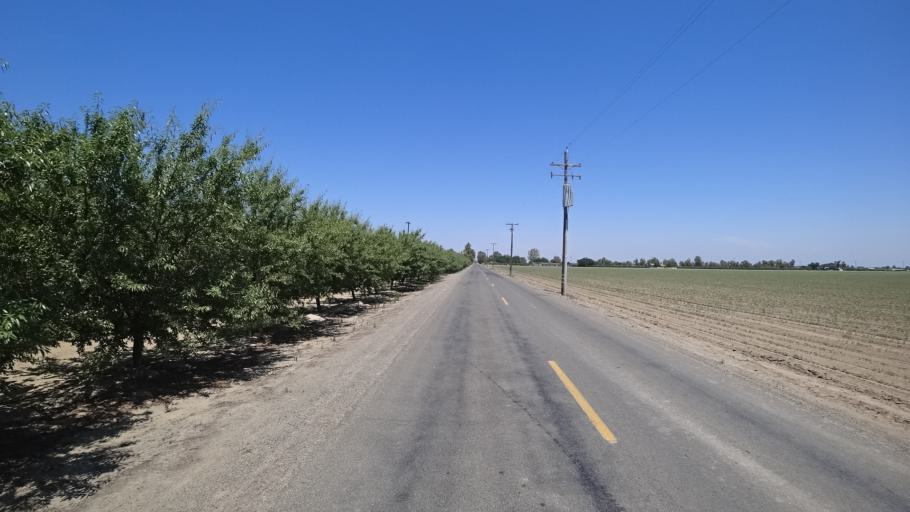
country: US
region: California
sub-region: Kings County
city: Lemoore
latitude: 36.2659
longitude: -119.7630
